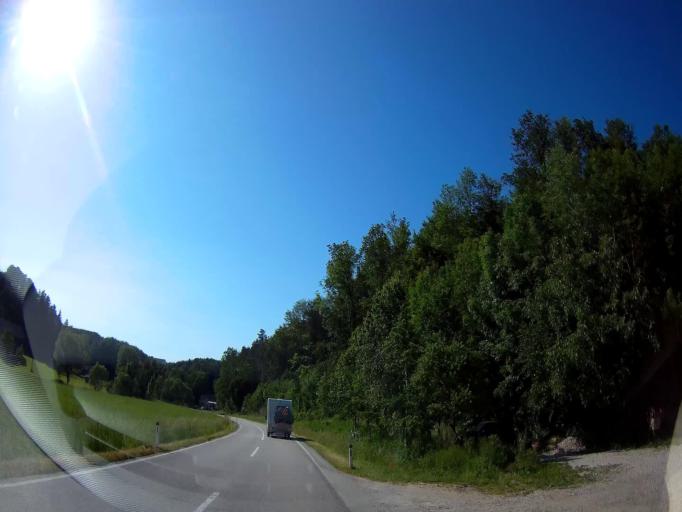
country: DE
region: Bavaria
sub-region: Lower Bavaria
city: Kirchdorf am Inn
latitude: 48.1391
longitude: 13.0183
